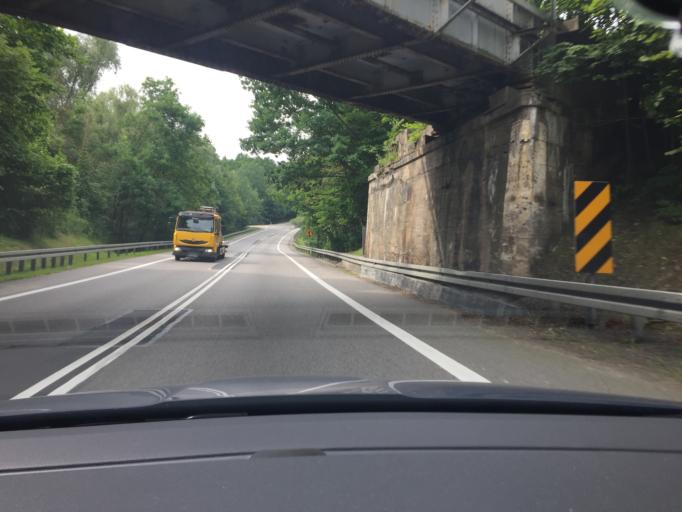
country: PL
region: Pomeranian Voivodeship
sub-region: Powiat starogardzki
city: Smetowo Graniczne
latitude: 53.7471
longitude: 18.7518
